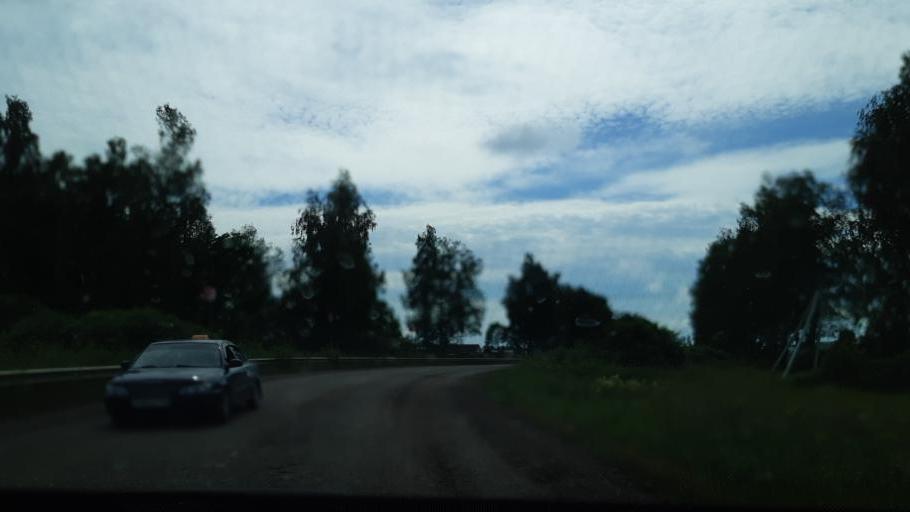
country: RU
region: Moskovskaya
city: Vereya
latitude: 55.3047
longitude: 36.1044
